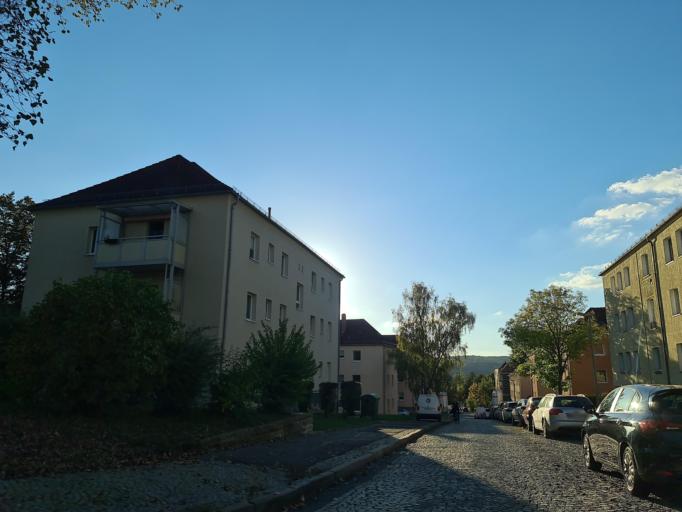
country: DE
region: Thuringia
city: Gera
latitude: 50.8908
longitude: 12.0857
